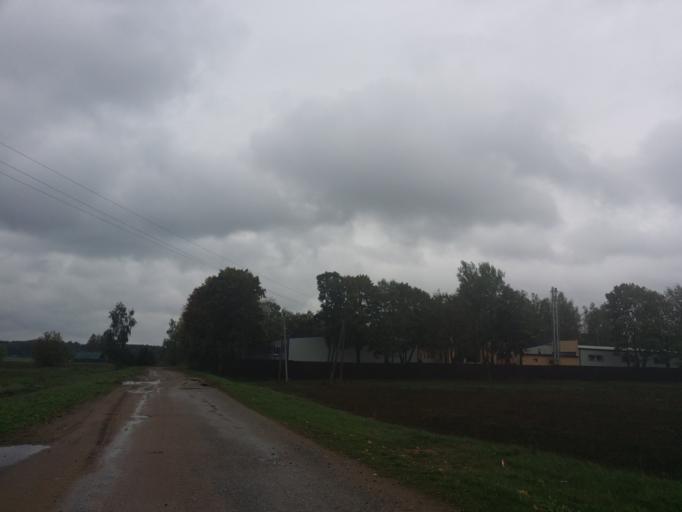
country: BY
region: Minsk
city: Chervyen'
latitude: 53.7644
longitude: 28.2517
